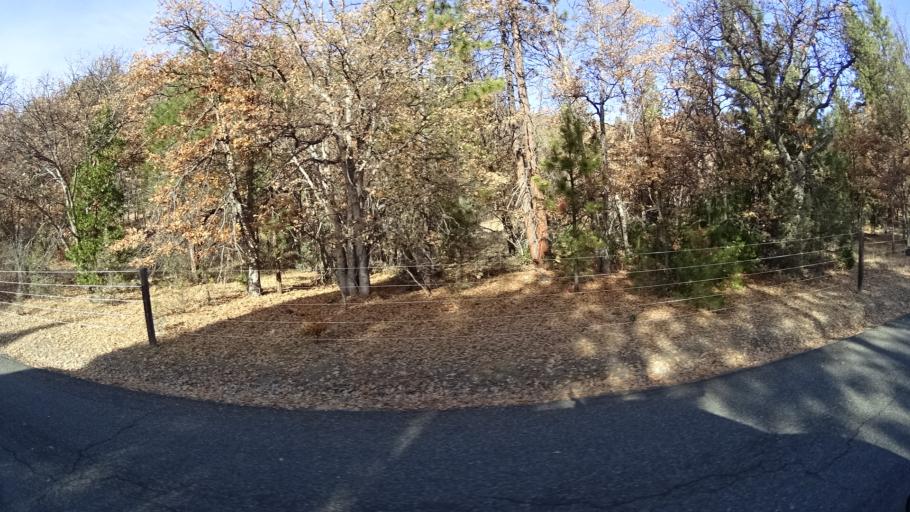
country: US
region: California
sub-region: Siskiyou County
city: Yreka
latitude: 41.6553
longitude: -122.6276
